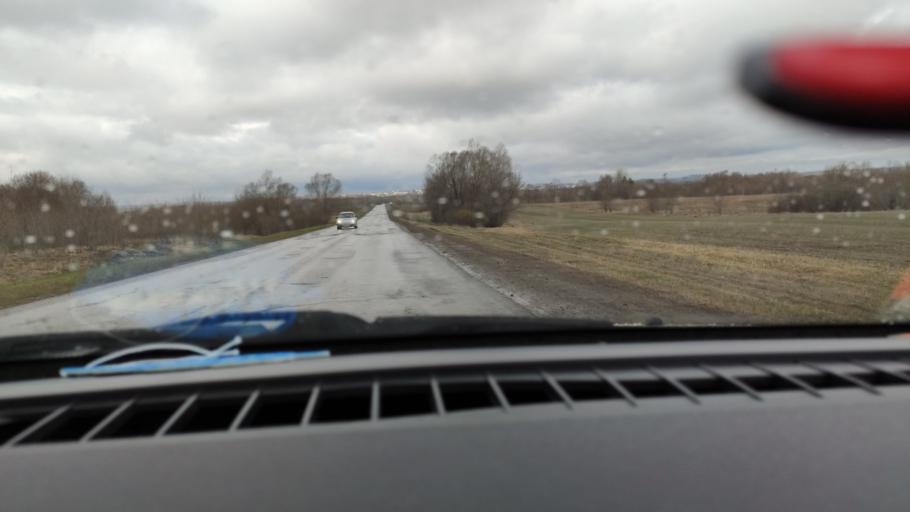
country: RU
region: Samara
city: Koshki
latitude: 54.1962
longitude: 50.5283
